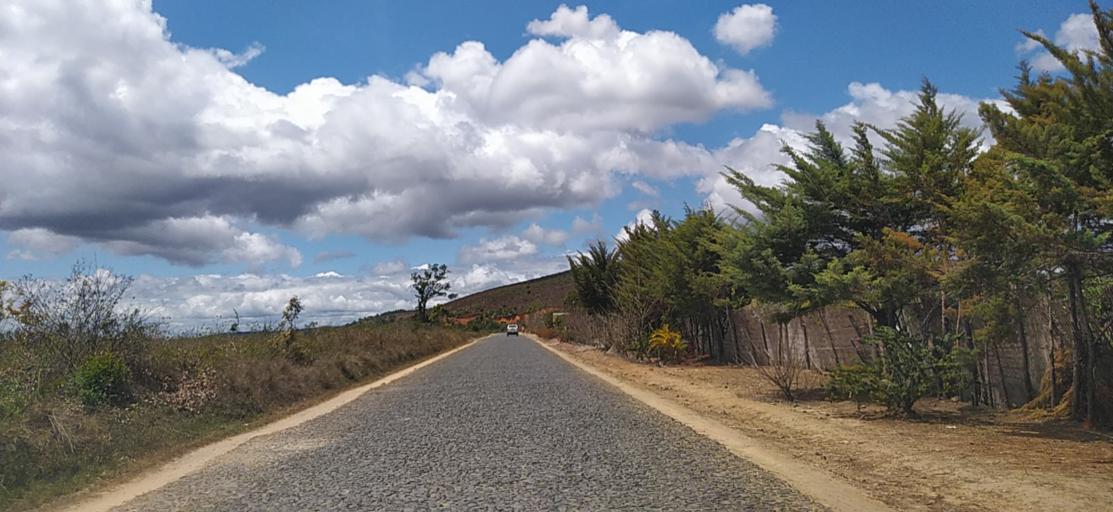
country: MG
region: Alaotra Mangoro
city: Moramanga
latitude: -18.7606
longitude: 48.2569
